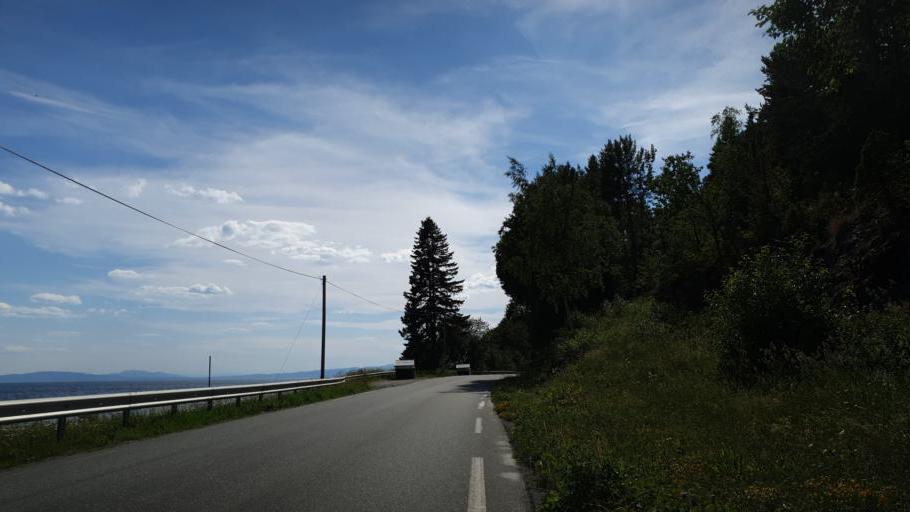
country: NO
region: Nord-Trondelag
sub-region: Leksvik
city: Leksvik
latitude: 63.6404
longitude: 10.5887
